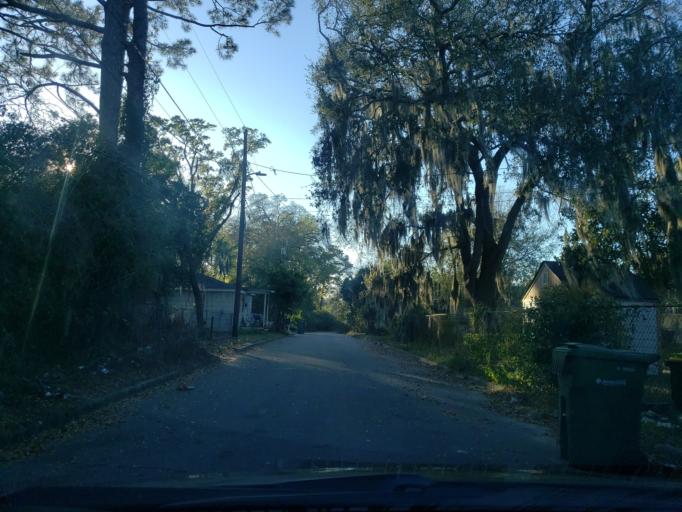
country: US
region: Georgia
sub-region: Chatham County
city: Thunderbolt
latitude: 32.0549
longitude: -81.0587
